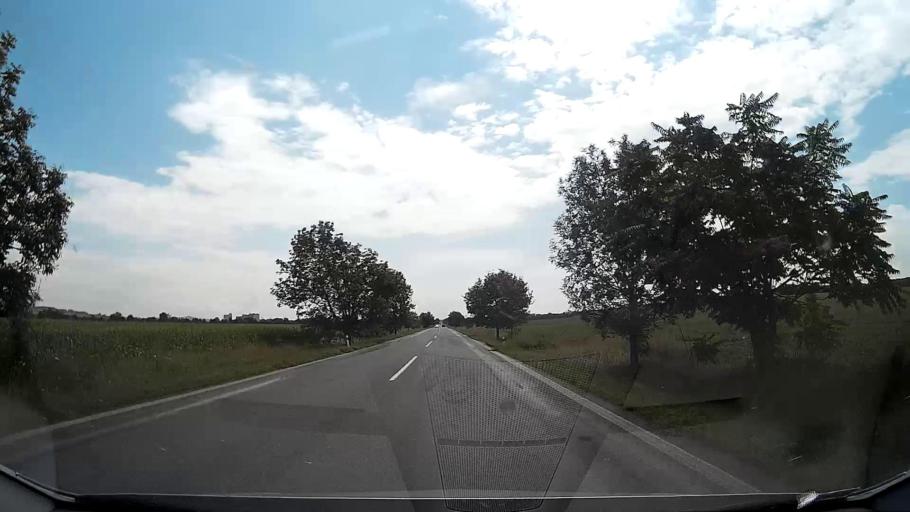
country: SK
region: Banskobystricky
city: Rimavska Sobota
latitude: 48.4028
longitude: 19.9823
